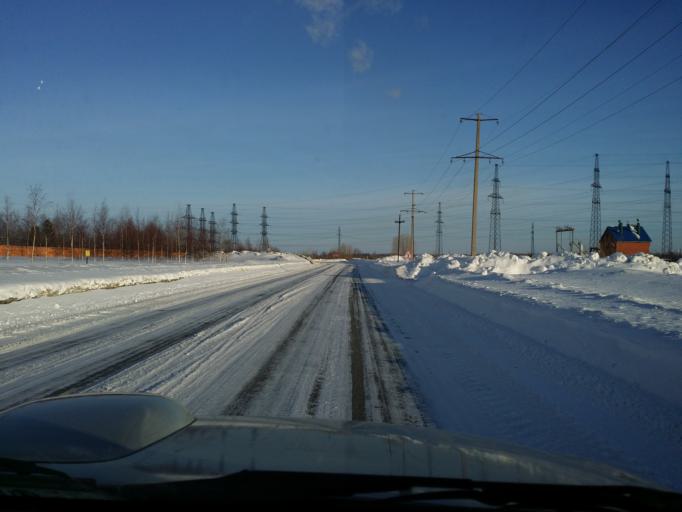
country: RU
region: Khanty-Mansiyskiy Avtonomnyy Okrug
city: Izluchinsk
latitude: 60.9734
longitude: 76.9410
